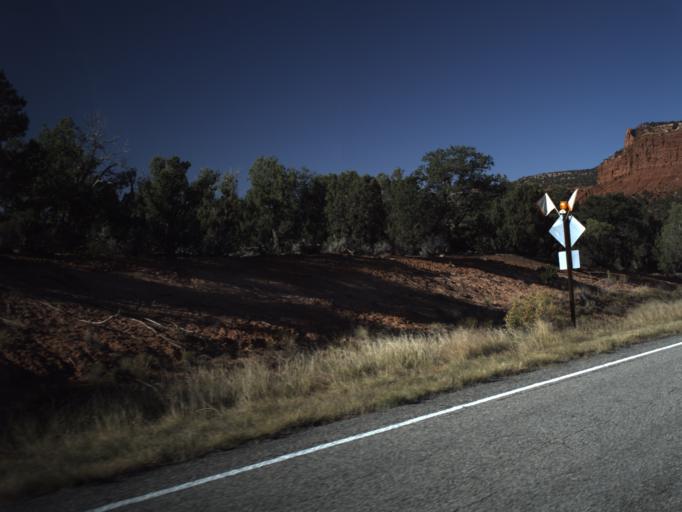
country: US
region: Utah
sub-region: San Juan County
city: Blanding
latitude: 37.5625
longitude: -110.0207
